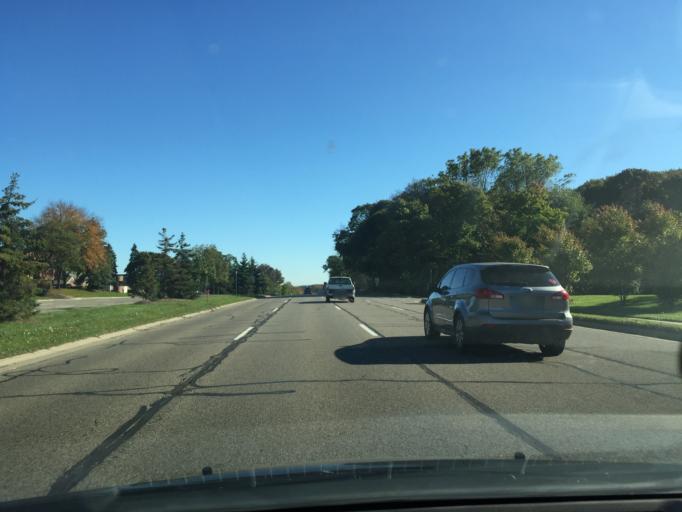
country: US
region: Michigan
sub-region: Oakland County
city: Bloomfield Hills
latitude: 42.6094
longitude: -83.2699
